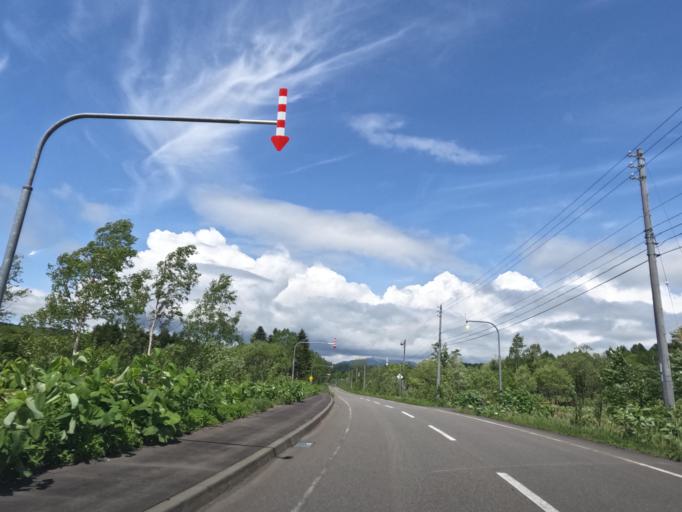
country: JP
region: Hokkaido
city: Tobetsu
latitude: 43.3813
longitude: 141.5768
